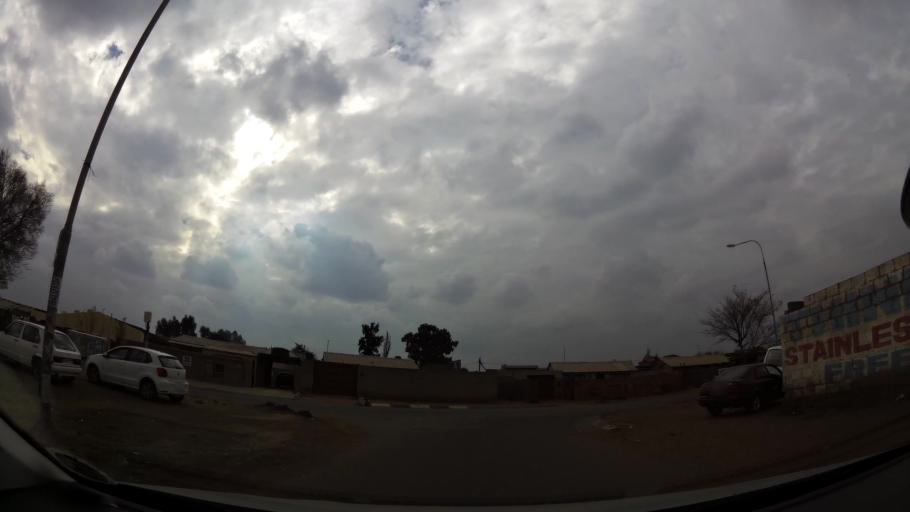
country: ZA
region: Gauteng
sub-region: City of Johannesburg Metropolitan Municipality
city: Soweto
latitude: -26.2643
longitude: 27.8504
